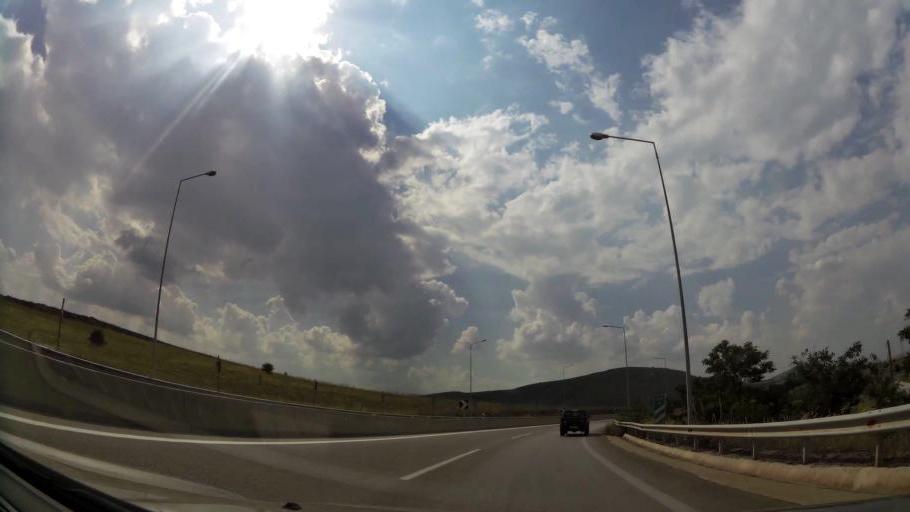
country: GR
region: West Macedonia
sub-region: Nomos Kozanis
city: Koila
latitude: 40.3420
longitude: 21.8075
